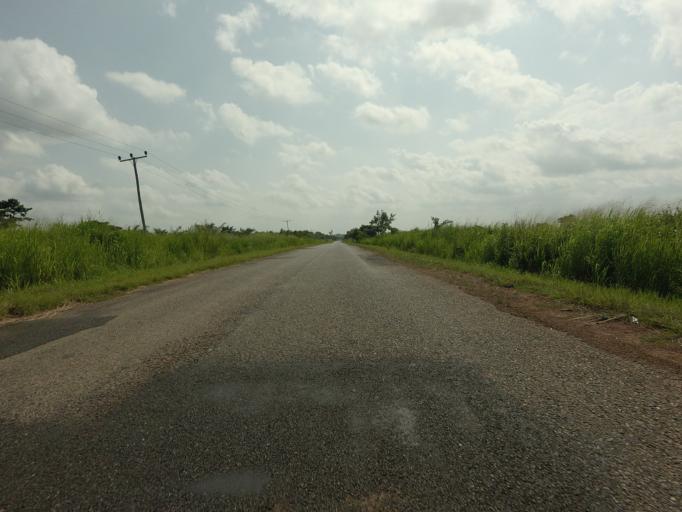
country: TG
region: Maritime
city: Tsevie
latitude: 6.3923
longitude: 0.8236
